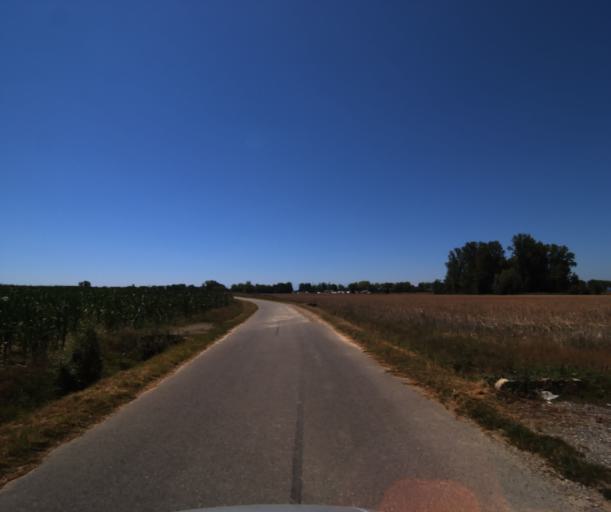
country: FR
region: Midi-Pyrenees
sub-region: Departement de la Haute-Garonne
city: Seysses
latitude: 43.4702
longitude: 1.2962
